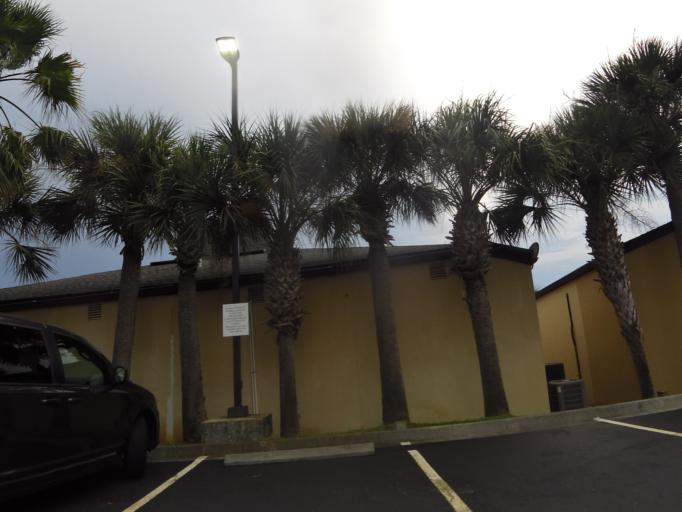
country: US
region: Florida
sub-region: Duval County
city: Jacksonville Beach
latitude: 30.2887
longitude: -81.4017
